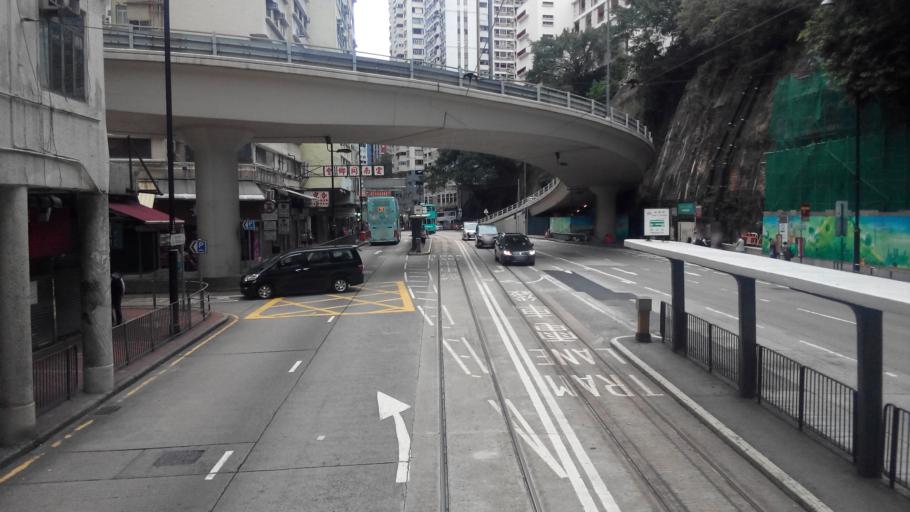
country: HK
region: Wanchai
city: Wan Chai
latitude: 22.2847
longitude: 114.1928
